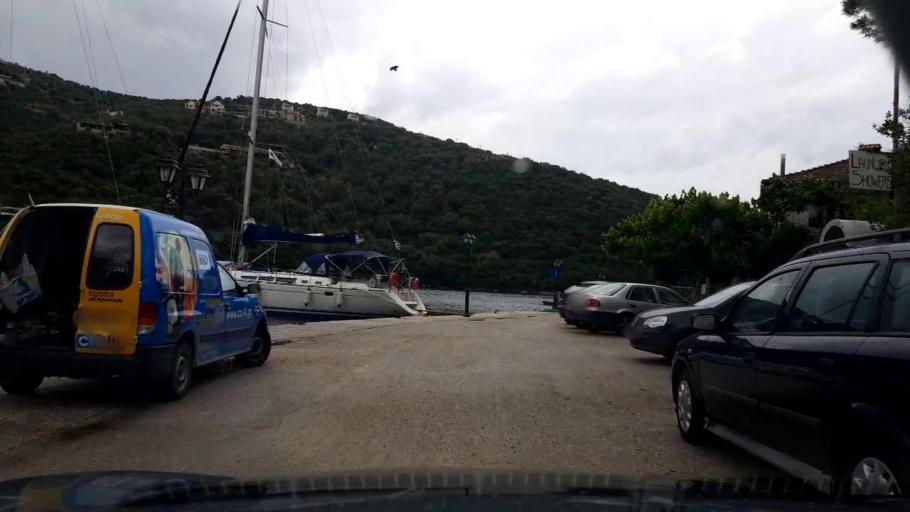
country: GR
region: Ionian Islands
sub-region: Lefkada
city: Nidri
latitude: 38.6219
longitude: 20.6838
